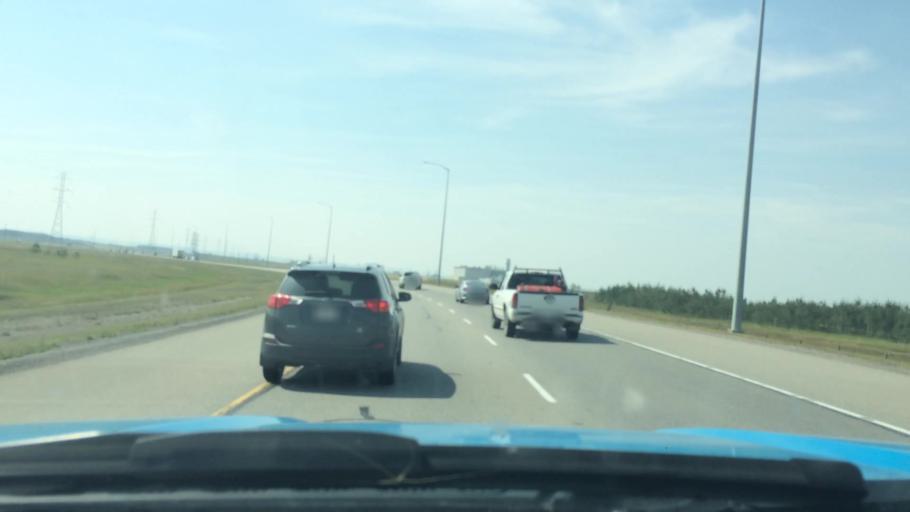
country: CA
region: Alberta
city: Airdrie
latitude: 51.1775
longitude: -113.9201
